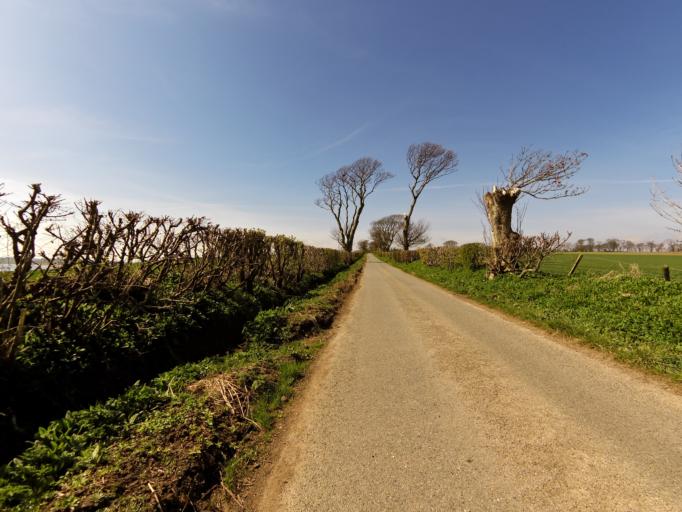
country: GB
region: Scotland
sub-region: Angus
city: Montrose
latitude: 56.6785
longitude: -2.4706
